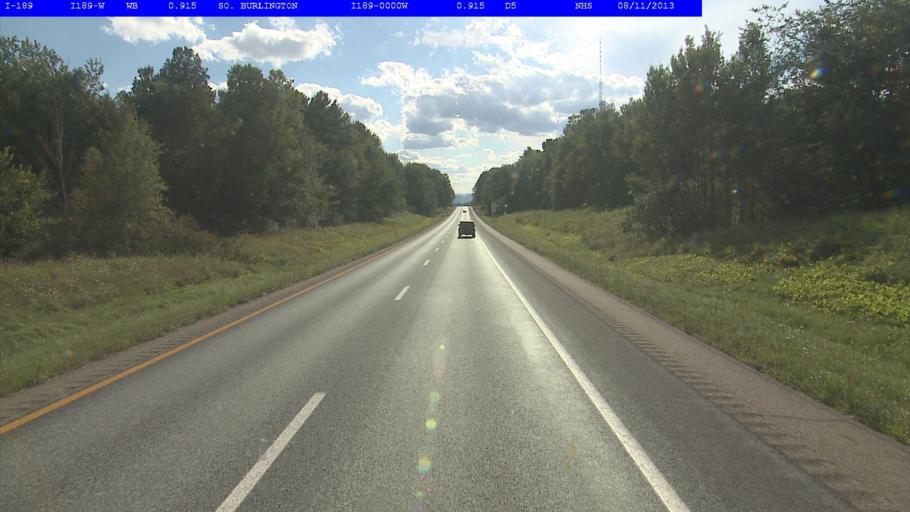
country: US
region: Vermont
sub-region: Chittenden County
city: South Burlington
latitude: 44.4511
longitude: -73.1920
